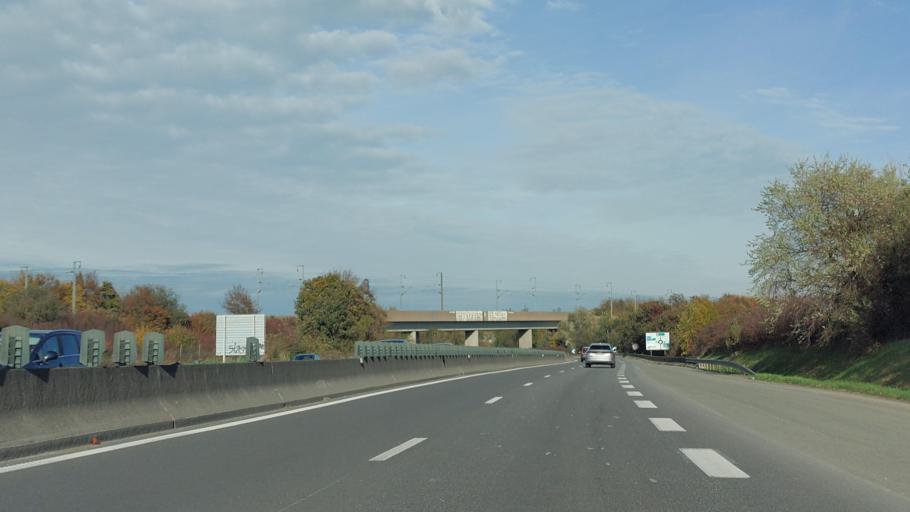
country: FR
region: Ile-de-France
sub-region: Departement du Val-d'Oise
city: Louvres
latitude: 49.0237
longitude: 2.4984
